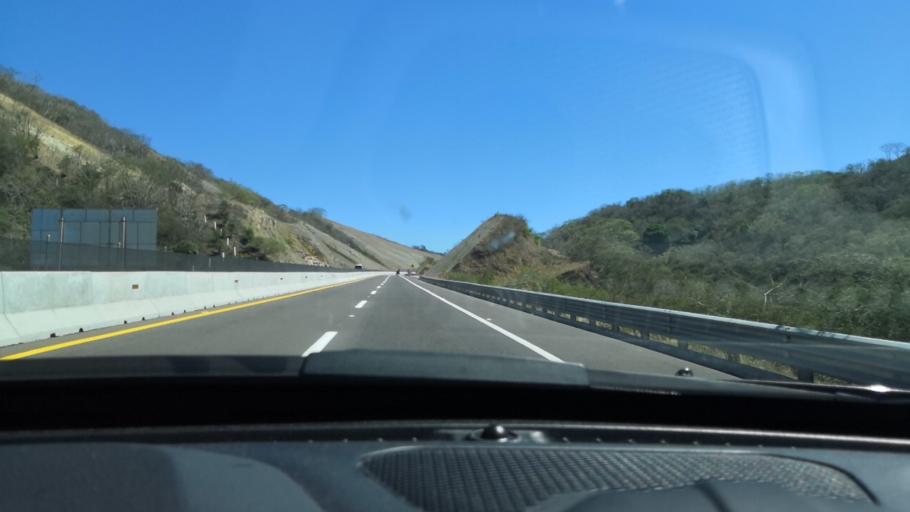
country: MX
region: Nayarit
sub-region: Compostela
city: Juan Escutia (Borbollon)
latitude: 21.1261
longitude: -104.8946
